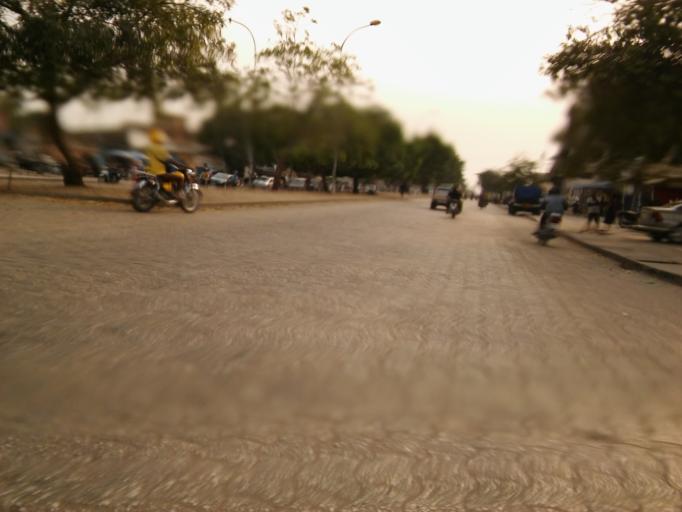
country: BJ
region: Littoral
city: Cotonou
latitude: 6.3693
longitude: 2.4069
